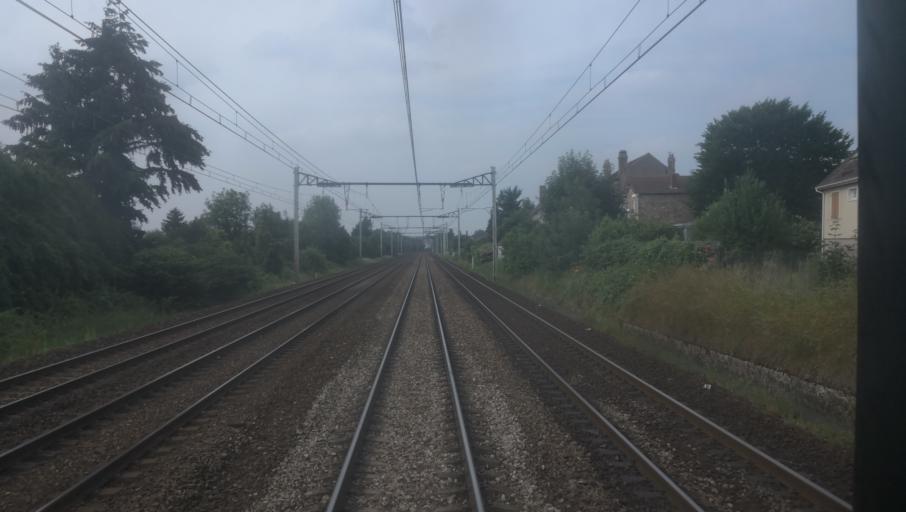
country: FR
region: Ile-de-France
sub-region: Departement de l'Essonne
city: Saint-Michel-sur-Orge
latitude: 48.6378
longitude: 2.3064
